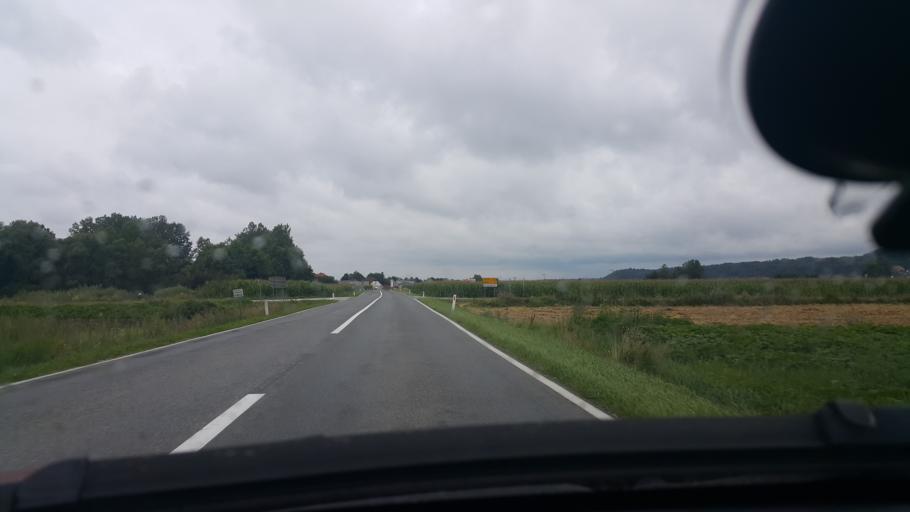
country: SI
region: Zavrc
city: Zavrc
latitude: 46.4149
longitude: 16.0443
